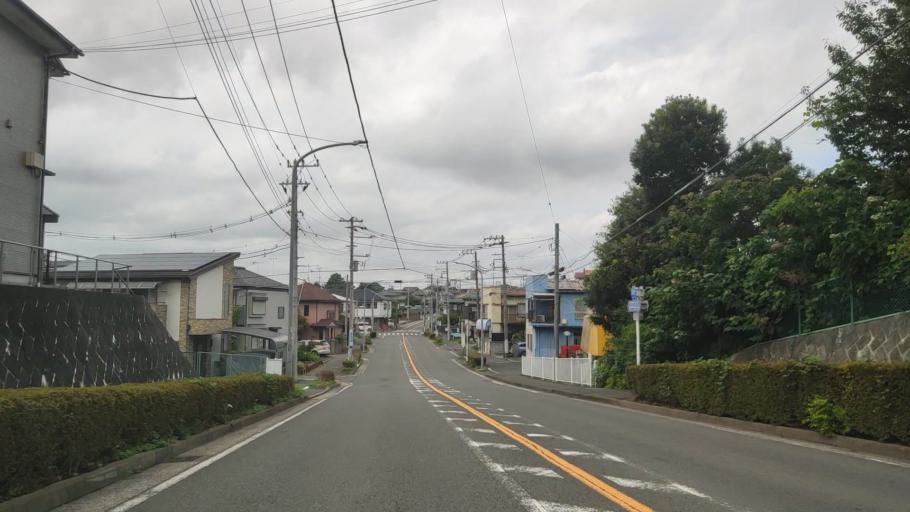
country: JP
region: Kanagawa
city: Minami-rinkan
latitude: 35.4737
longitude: 139.4776
